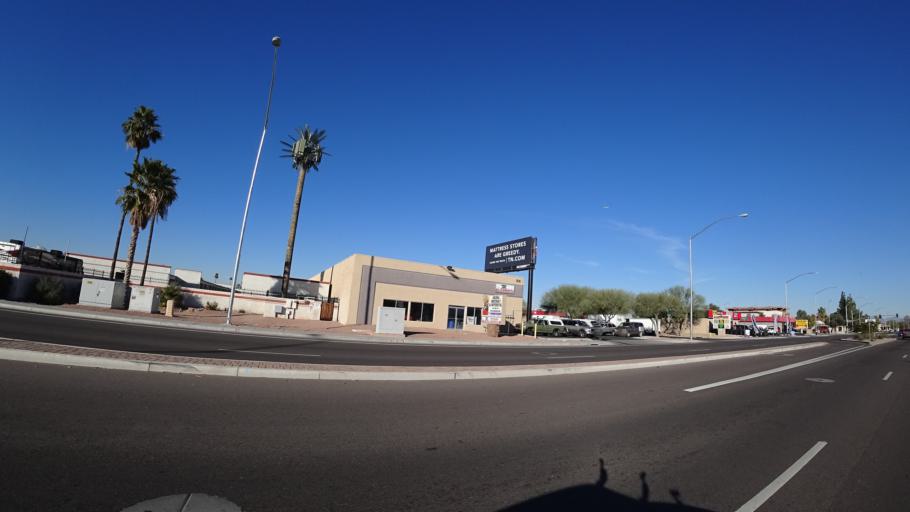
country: US
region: Arizona
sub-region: Maricopa County
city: Mesa
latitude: 33.3933
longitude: -111.8252
